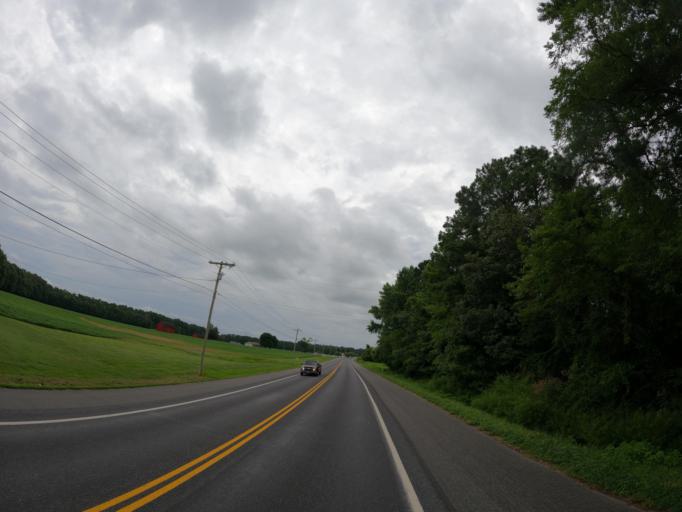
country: US
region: Maryland
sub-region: Saint Mary's County
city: Lexington Park
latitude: 38.1853
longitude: -76.5138
